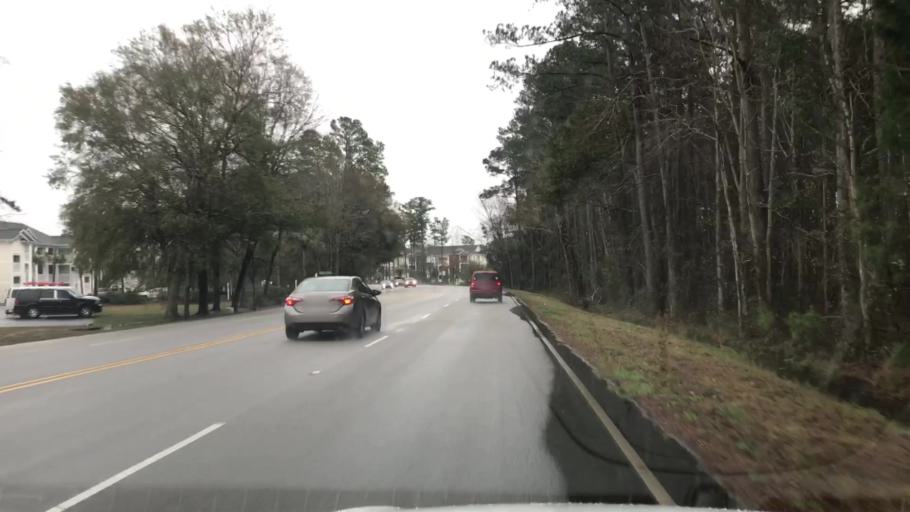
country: US
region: South Carolina
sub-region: Horry County
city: Forestbrook
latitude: 33.7214
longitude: -78.9254
